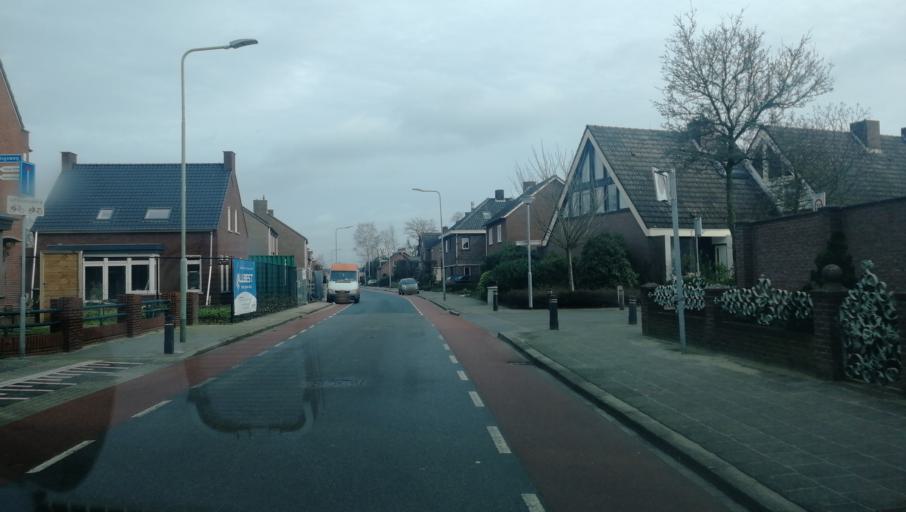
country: NL
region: Limburg
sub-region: Gemeente Venlo
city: Tegelen
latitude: 51.3150
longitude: 6.1195
